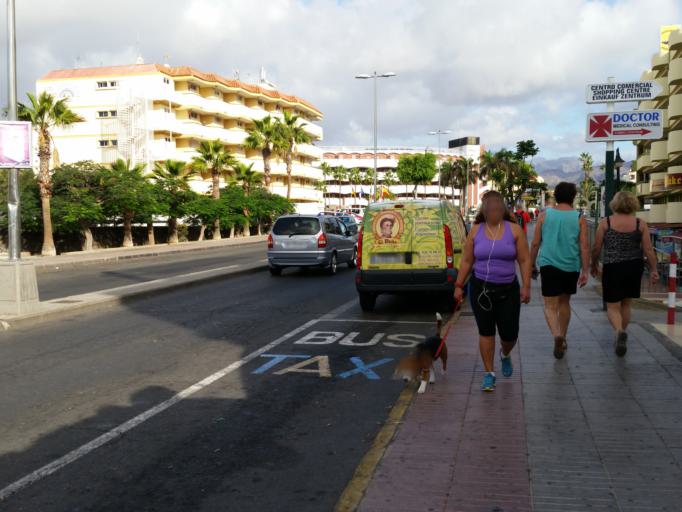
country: ES
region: Canary Islands
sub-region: Provincia de Las Palmas
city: Playa del Ingles
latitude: 27.7586
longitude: -15.5789
